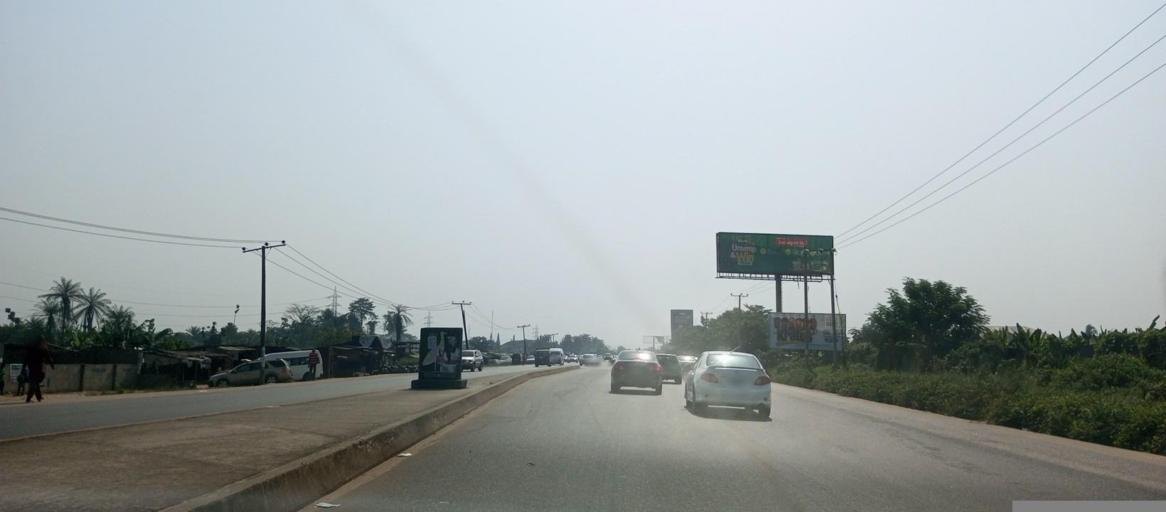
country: NG
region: Rivers
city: Emuoha
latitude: 4.8966
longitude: 6.9101
